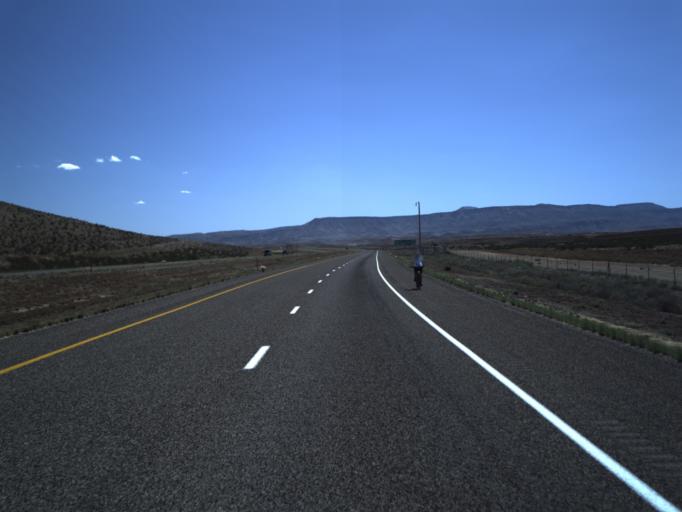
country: US
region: Utah
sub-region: Washington County
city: Saint George
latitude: 37.0145
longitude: -113.5938
